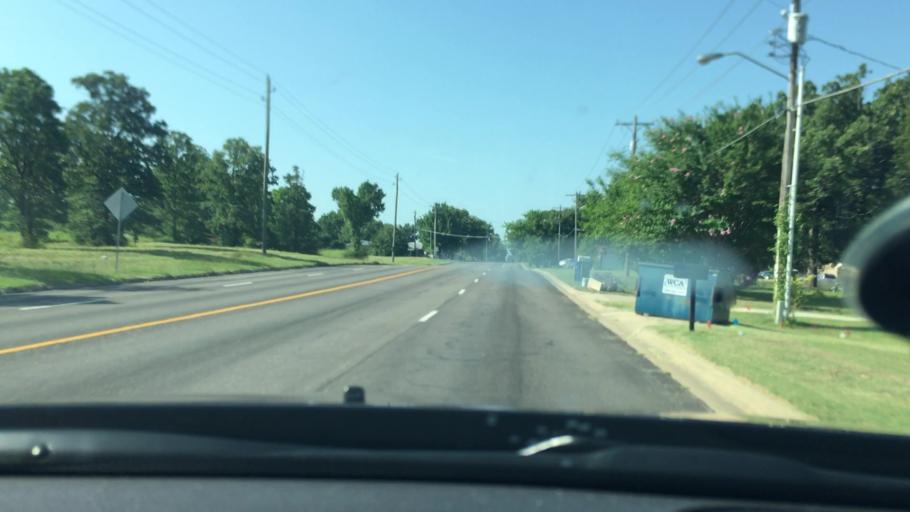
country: US
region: Oklahoma
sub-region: Pontotoc County
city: Ada
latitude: 34.7763
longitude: -96.6349
